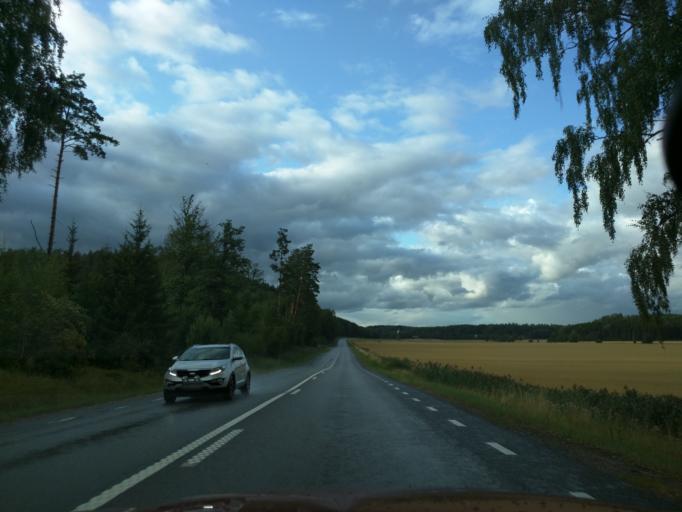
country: SE
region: Soedermanland
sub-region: Nykopings Kommun
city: Nykoping
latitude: 58.8034
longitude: 17.0823
